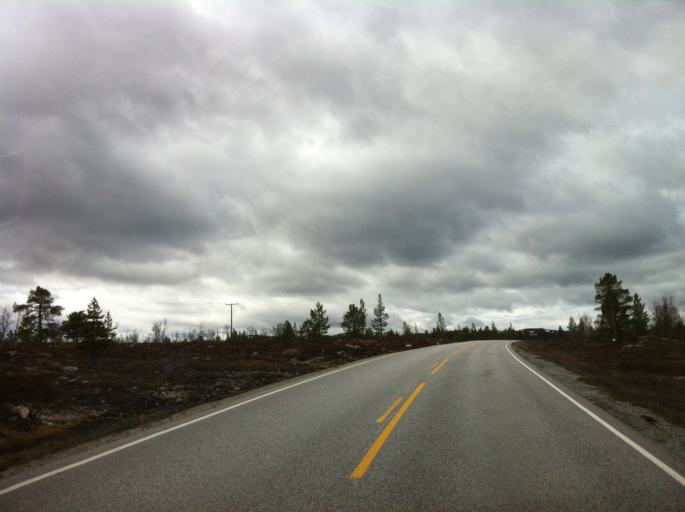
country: NO
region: Sor-Trondelag
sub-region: Roros
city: Roros
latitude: 62.6045
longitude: 11.8441
